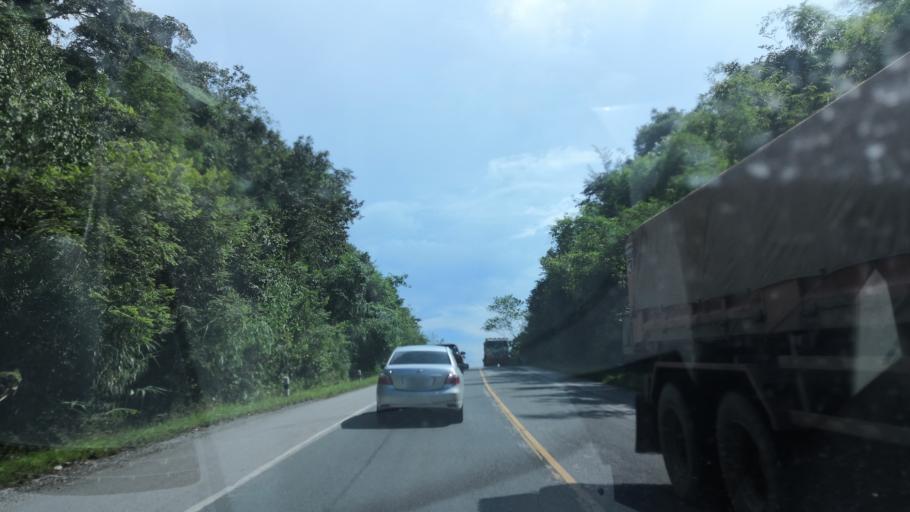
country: TH
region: Chiang Rai
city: Wiang Pa Pao
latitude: 19.4544
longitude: 99.4966
